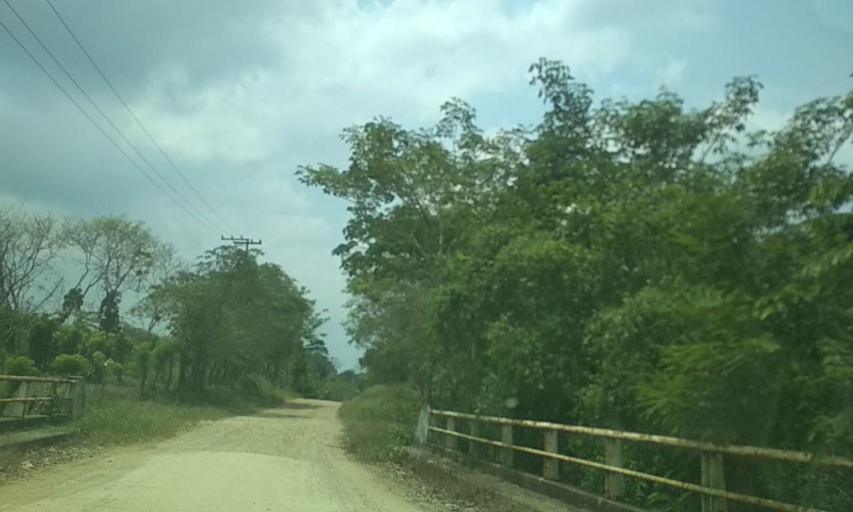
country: MX
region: Tabasco
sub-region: Huimanguillo
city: Francisco Rueda
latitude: 17.5935
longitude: -93.7940
